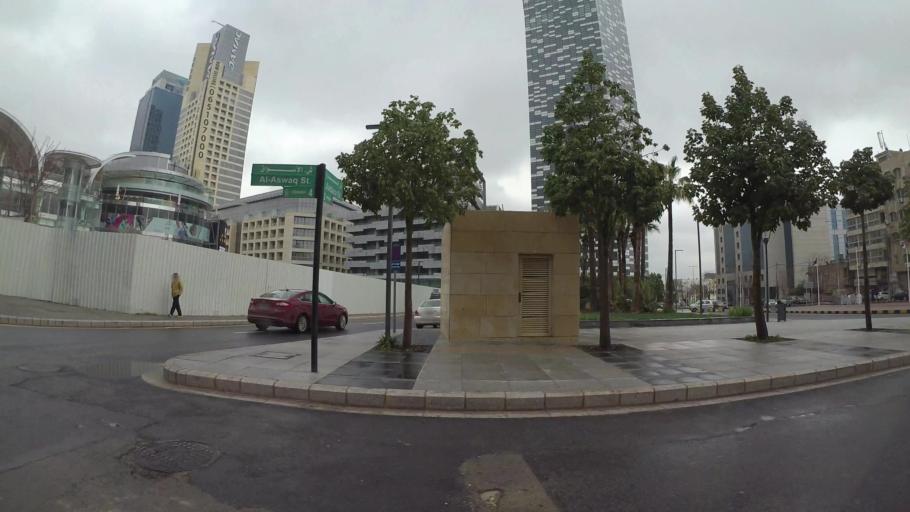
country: JO
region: Amman
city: Amman
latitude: 31.9627
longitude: 35.9072
